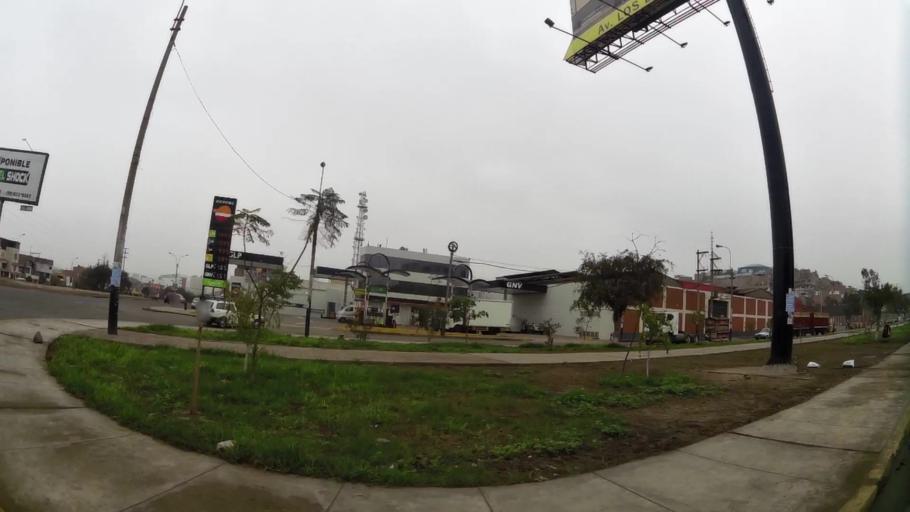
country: PE
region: Lima
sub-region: Lima
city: Surco
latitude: -12.1613
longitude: -76.9792
